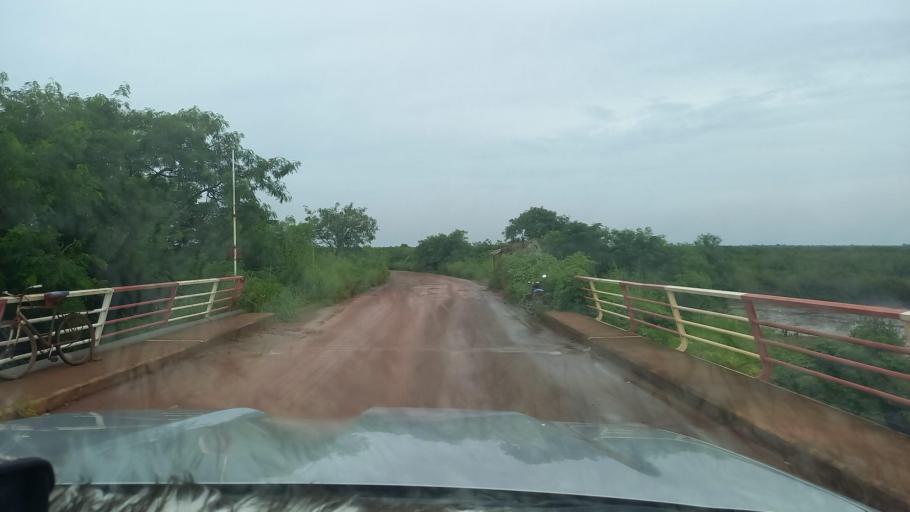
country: SN
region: Ziguinchor
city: Ziguinchor
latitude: 12.5923
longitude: -16.2627
